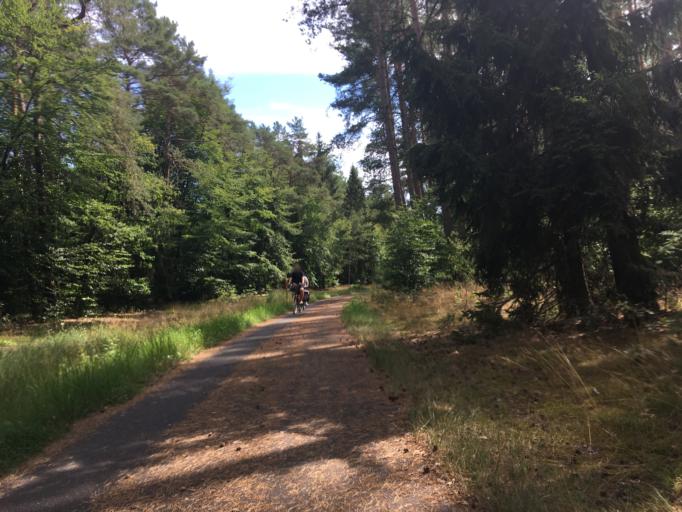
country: DE
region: Brandenburg
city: Rheinsberg
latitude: 53.0655
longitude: 12.9088
